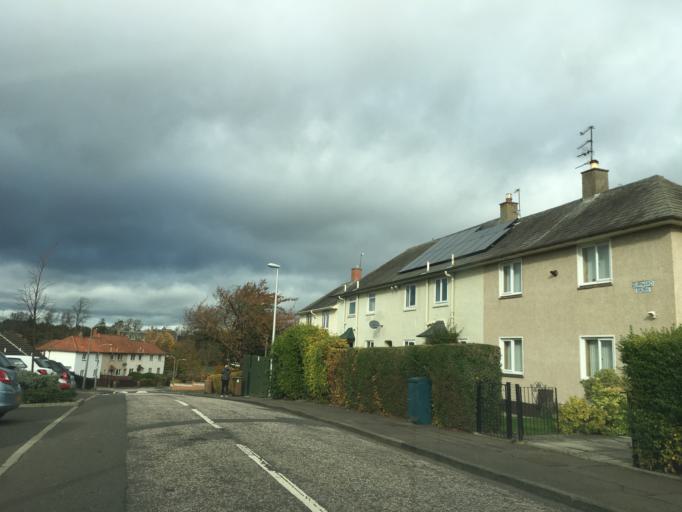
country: GB
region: Scotland
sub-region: Midlothian
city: Loanhead
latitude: 55.9223
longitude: -3.1557
